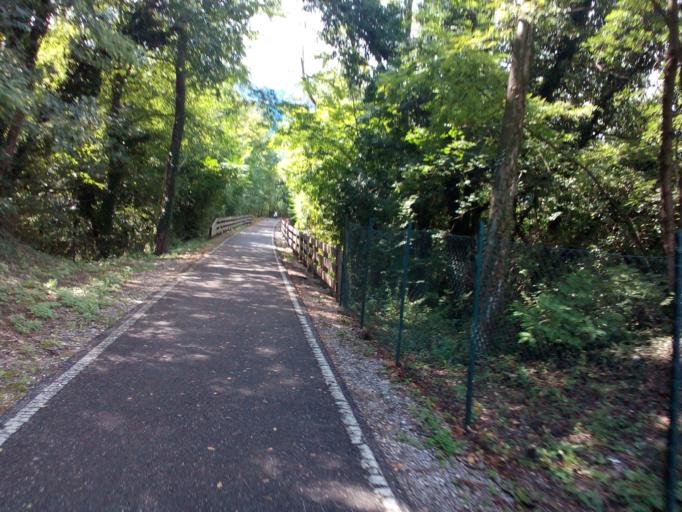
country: IT
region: Trentino-Alto Adige
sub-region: Bolzano
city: Cornaiano
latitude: 46.4762
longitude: 11.2856
